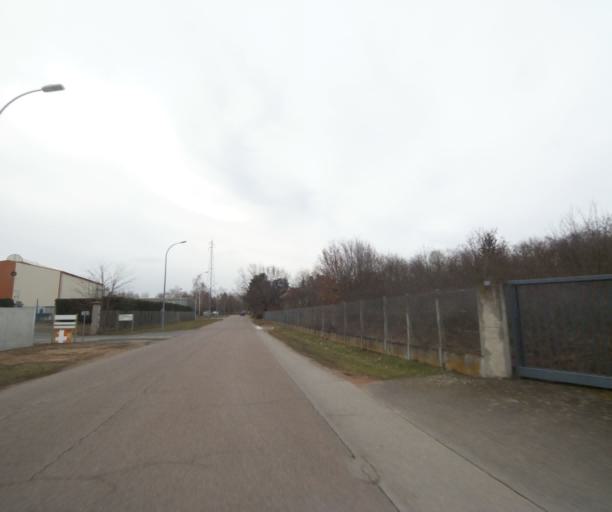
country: FR
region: Rhone-Alpes
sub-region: Departement de la Loire
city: Perreux
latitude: 46.0549
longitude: 4.0979
